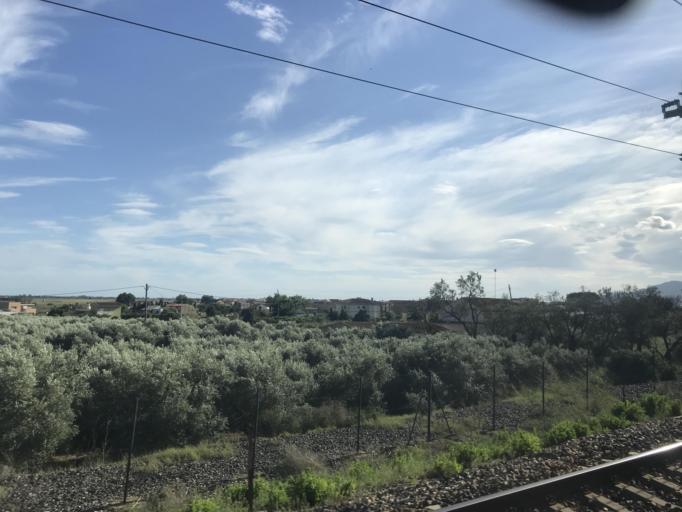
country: ES
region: Catalonia
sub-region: Provincia de Tarragona
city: Camarles
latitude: 40.7629
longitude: 0.6509
